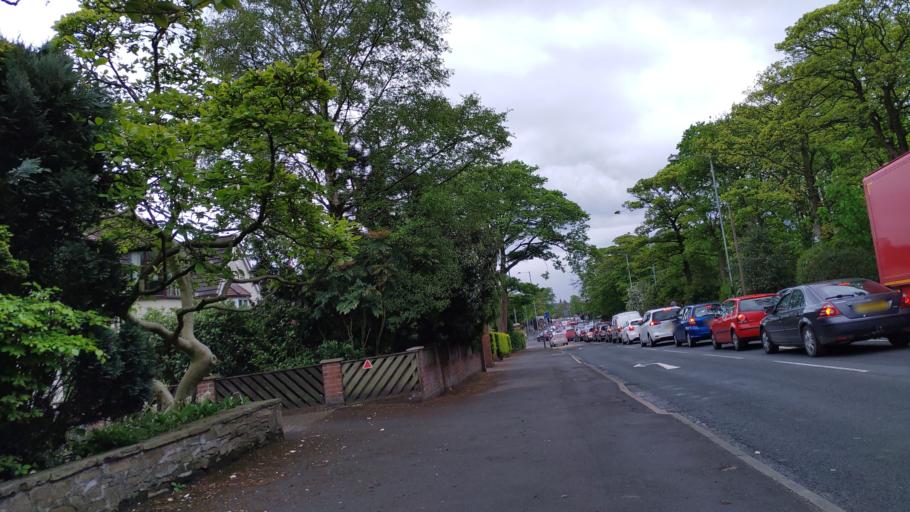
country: GB
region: England
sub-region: Lancashire
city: Chorley
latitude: 53.6698
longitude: -2.6322
